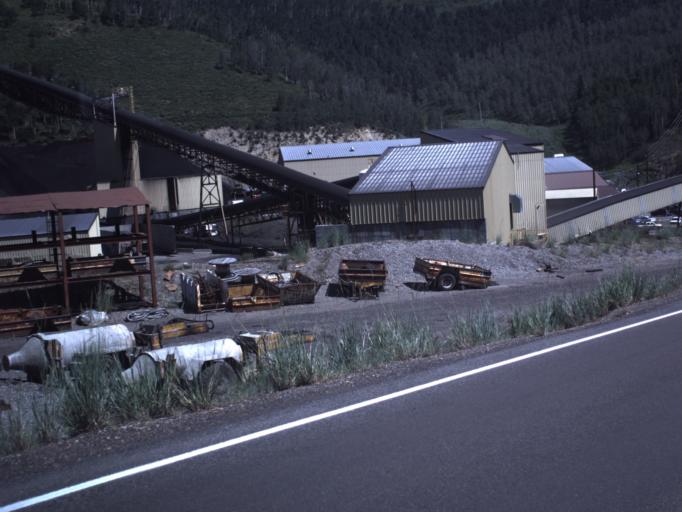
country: US
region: Utah
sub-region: Sanpete County
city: Fairview
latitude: 39.6827
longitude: -111.2057
